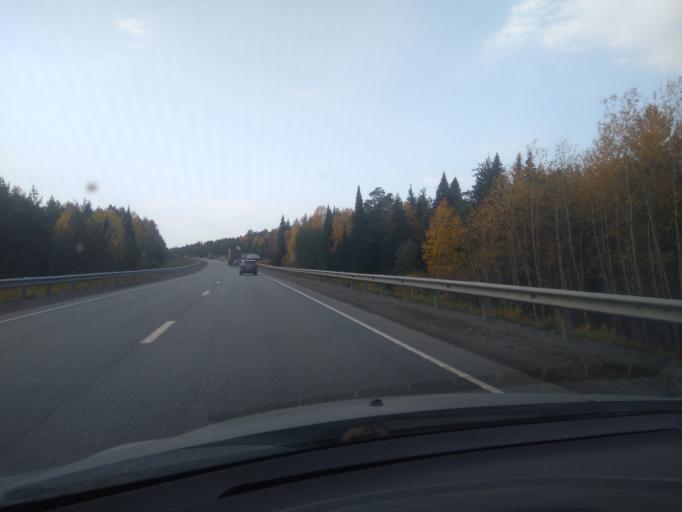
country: RU
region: Sverdlovsk
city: Druzhinino
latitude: 56.8226
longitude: 59.5738
